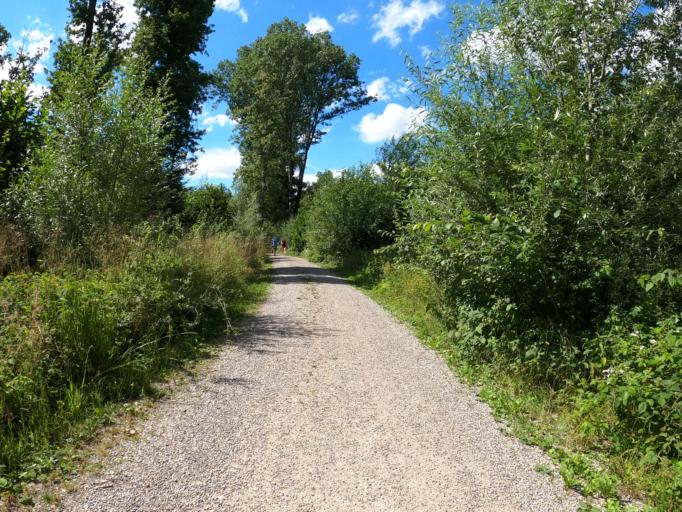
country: DE
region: Bavaria
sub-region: Swabia
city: Leipheim
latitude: 48.4213
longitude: 10.2094
